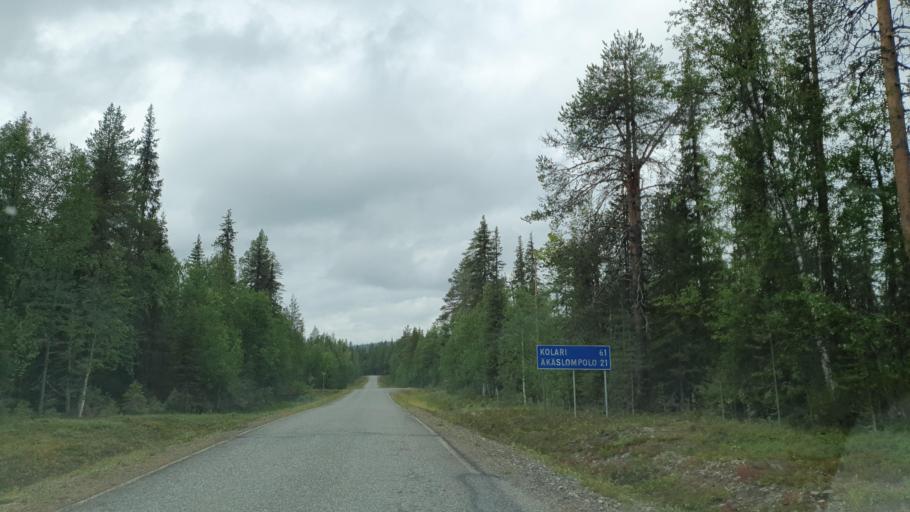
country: FI
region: Lapland
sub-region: Tunturi-Lappi
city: Kittilae
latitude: 67.7401
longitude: 24.2982
